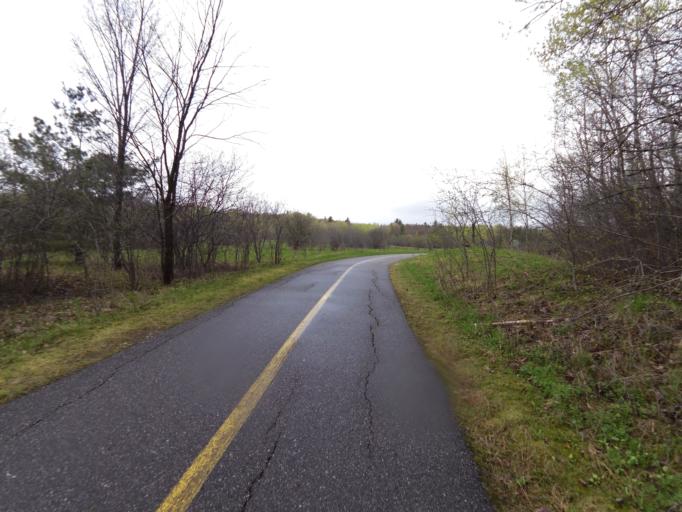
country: CA
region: Quebec
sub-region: Outaouais
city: Gatineau
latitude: 45.4643
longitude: -75.7875
